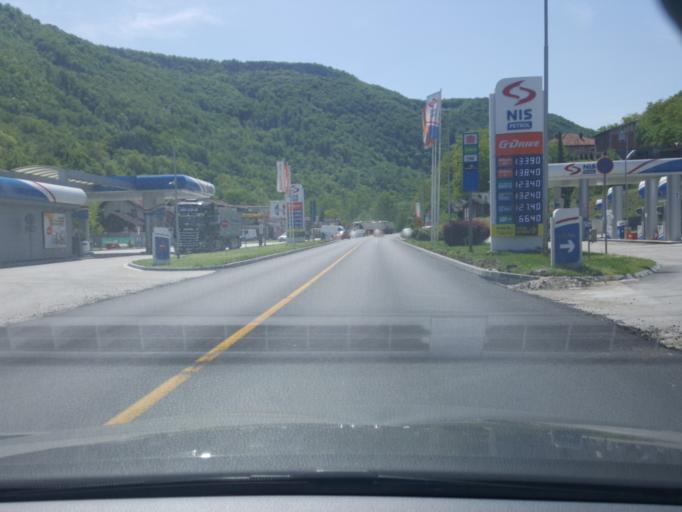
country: RS
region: Central Serbia
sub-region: Zlatiborski Okrug
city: Uzice
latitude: 43.8371
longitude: 19.8830
